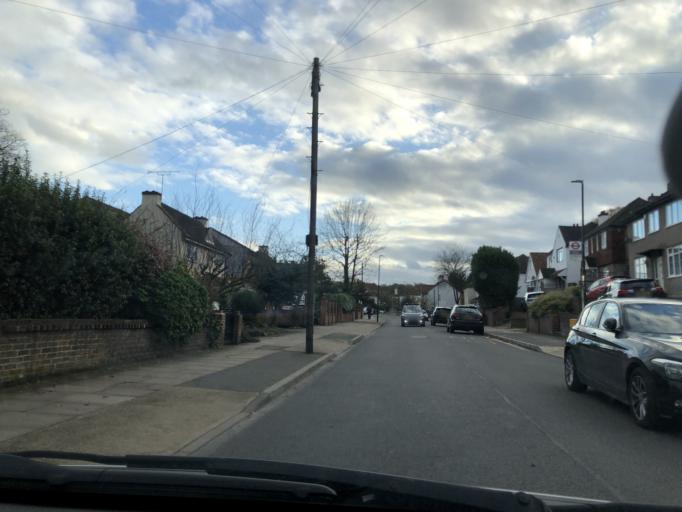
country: GB
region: England
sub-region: Greater London
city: Bexley
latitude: 51.4346
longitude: 0.1660
